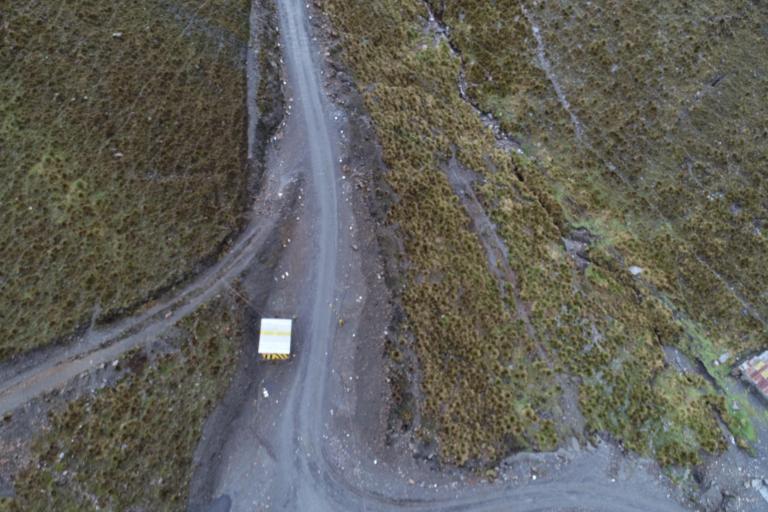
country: BO
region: La Paz
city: Sorata
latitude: -15.6632
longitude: -68.5126
